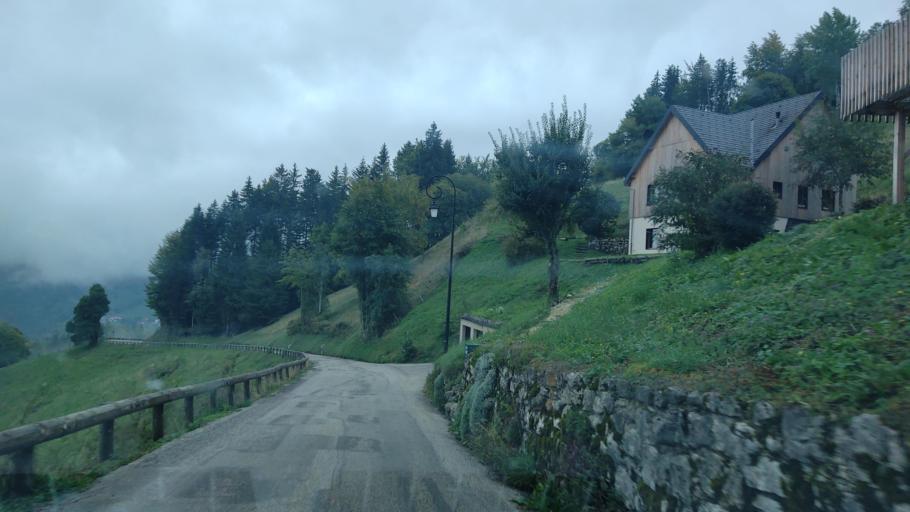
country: FR
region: Rhone-Alpes
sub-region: Departement de la Savoie
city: Les Echelles
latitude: 45.4130
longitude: 5.8391
